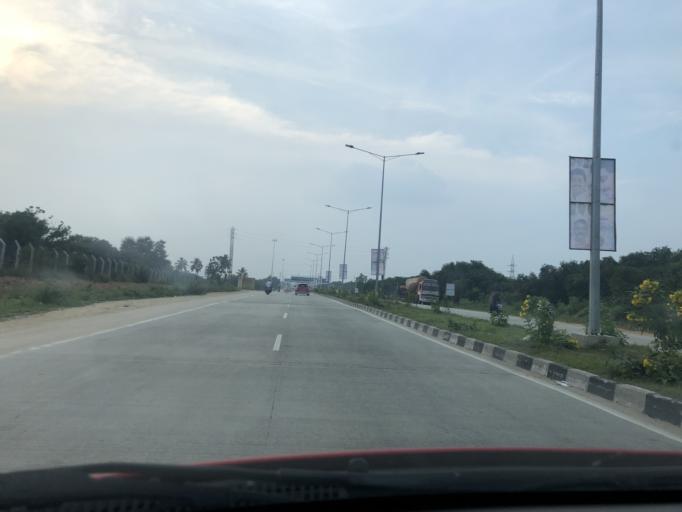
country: IN
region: Andhra Pradesh
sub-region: Chittoor
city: Chittoor
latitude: 13.1945
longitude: 79.0220
